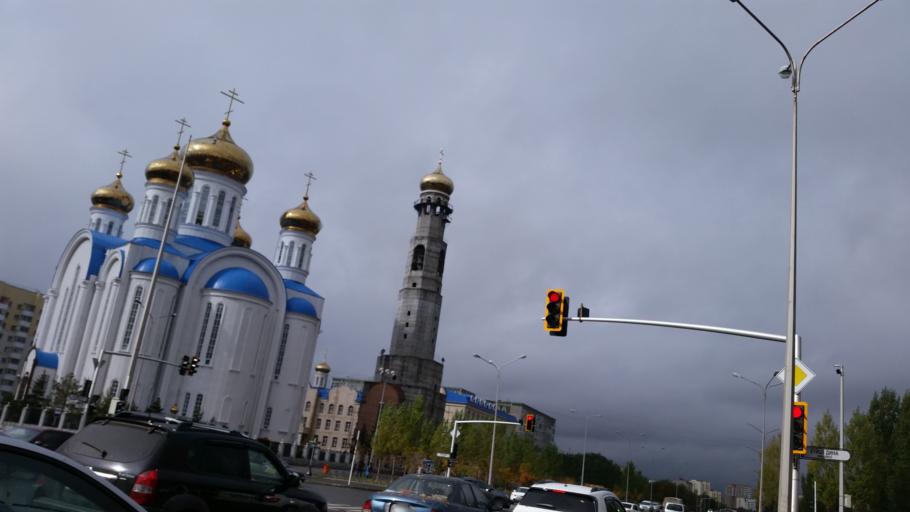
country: KZ
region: Astana Qalasy
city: Astana
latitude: 51.1491
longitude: 71.4832
